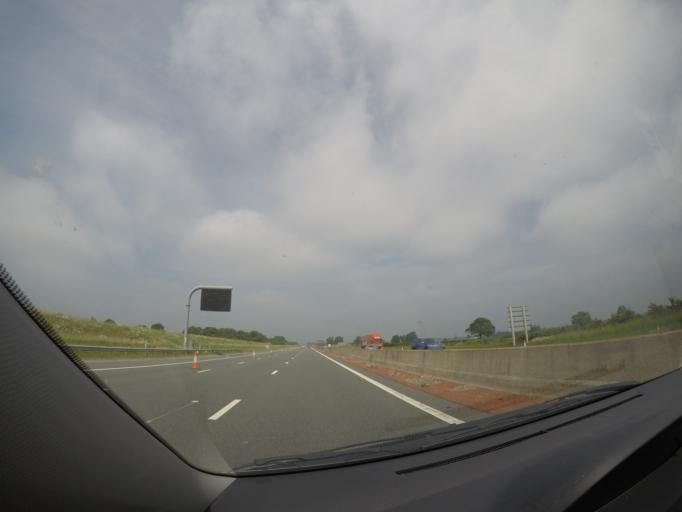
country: GB
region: England
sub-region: North Yorkshire
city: Ripon
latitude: 54.1900
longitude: -1.4635
